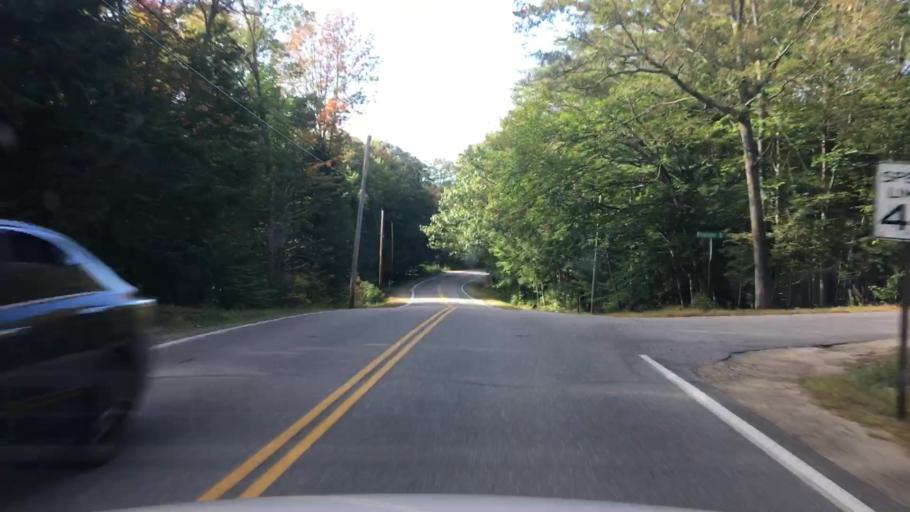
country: US
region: Maine
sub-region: Sagadahoc County
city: Topsham
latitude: 43.9393
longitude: -70.0237
